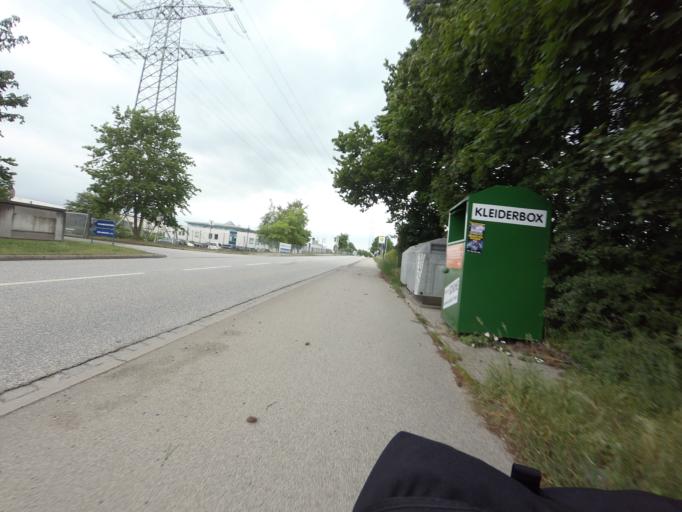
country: DE
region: Mecklenburg-Vorpommern
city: Selmsdorf
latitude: 53.8987
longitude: 10.7967
